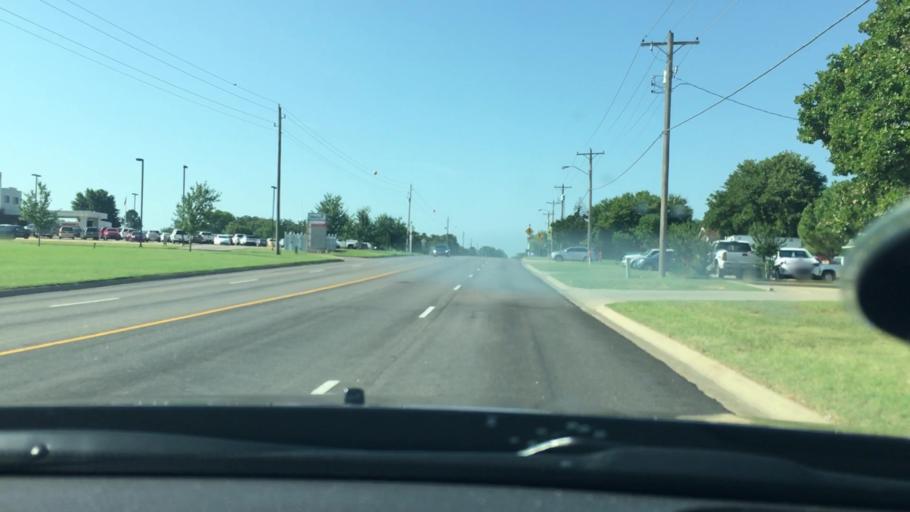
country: US
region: Oklahoma
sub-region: Pontotoc County
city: Ada
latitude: 34.7797
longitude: -96.6349
